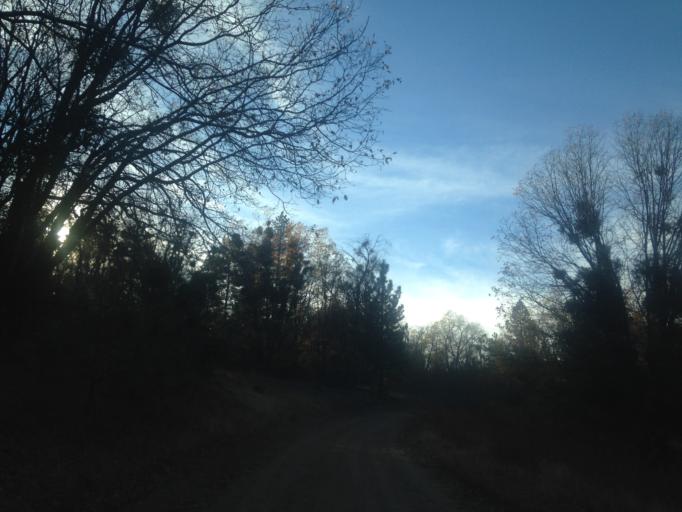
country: US
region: California
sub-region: San Bernardino County
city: Yucaipa
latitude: 34.1300
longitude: -117.0087
